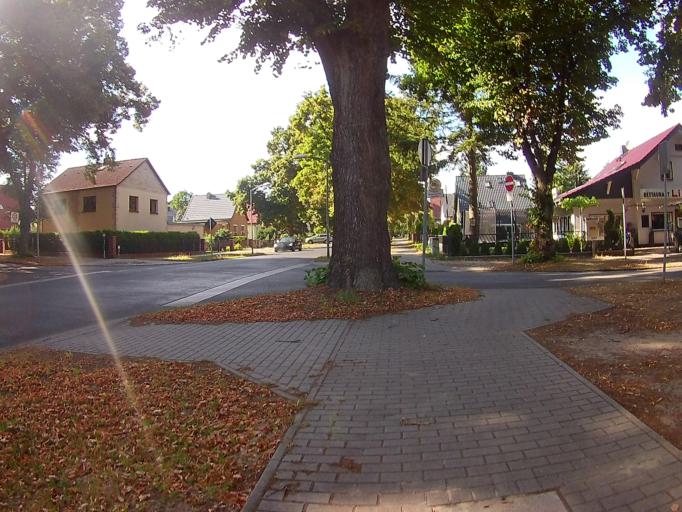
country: DE
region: Brandenburg
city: Zeuthen
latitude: 52.3727
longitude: 13.6023
